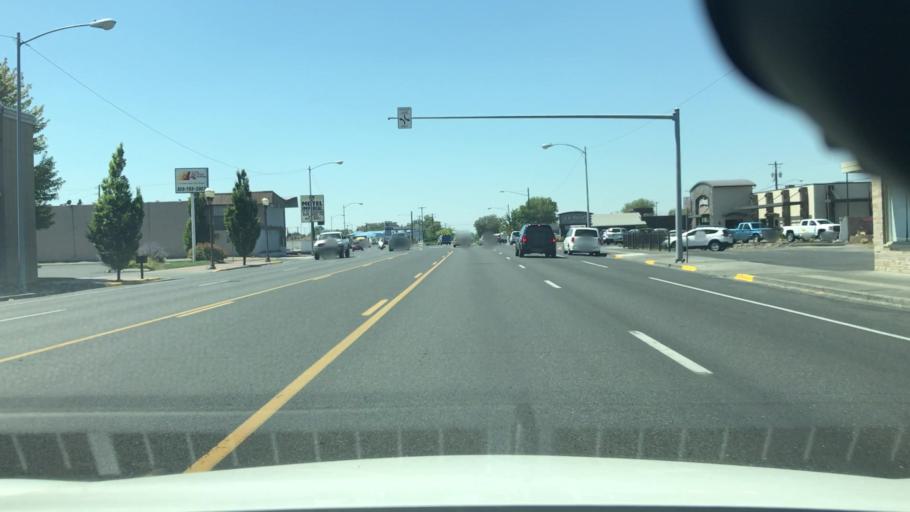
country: US
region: Washington
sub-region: Grant County
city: Moses Lake
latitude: 47.1266
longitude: -119.2879
